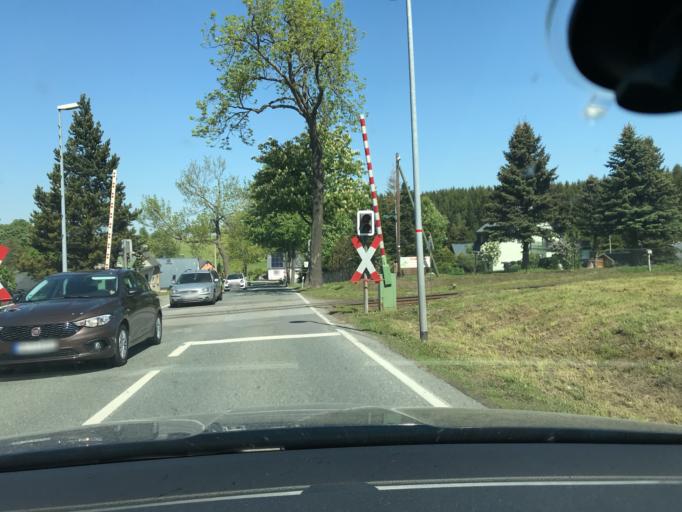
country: CZ
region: Ustecky
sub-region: Okres Chomutov
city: Vejprty
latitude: 50.4673
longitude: 12.9891
